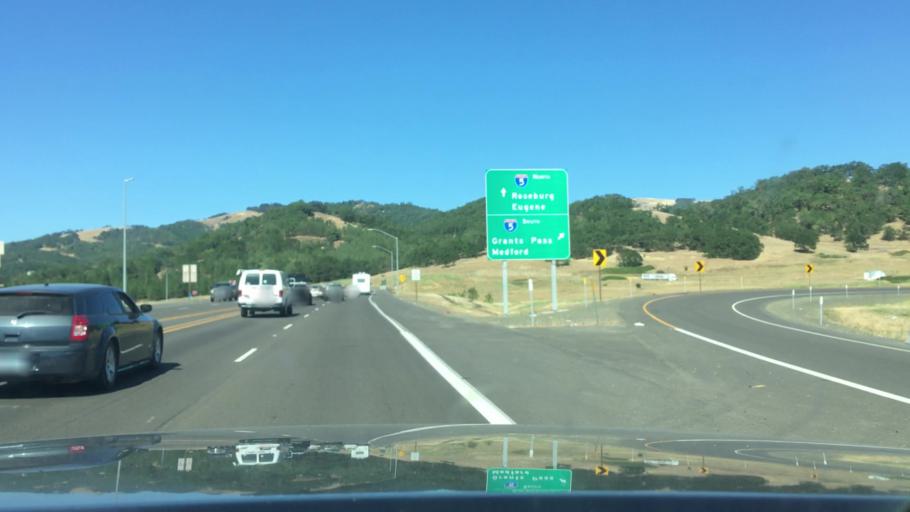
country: US
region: Oregon
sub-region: Douglas County
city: Green
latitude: 43.1514
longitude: -123.3681
